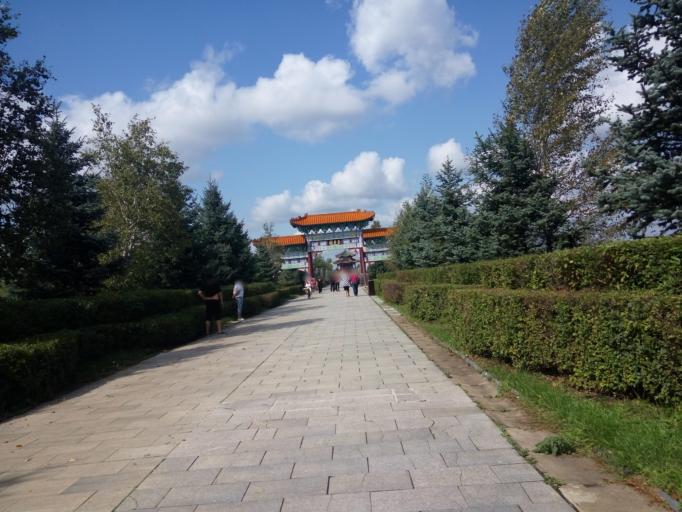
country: CN
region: Heilongjiang Sheng
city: Erjing
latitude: 48.6505
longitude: 126.1488
